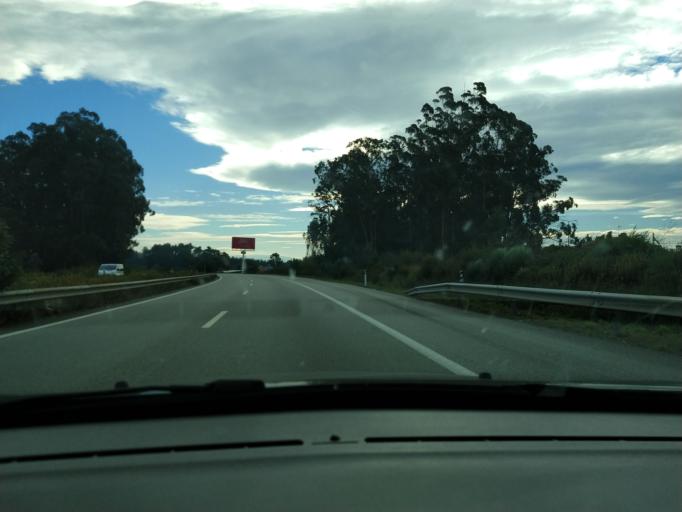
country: PT
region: Aveiro
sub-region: Albergaria-A-Velha
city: Albergaria-a-Velha
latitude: 40.6829
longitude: -8.5350
